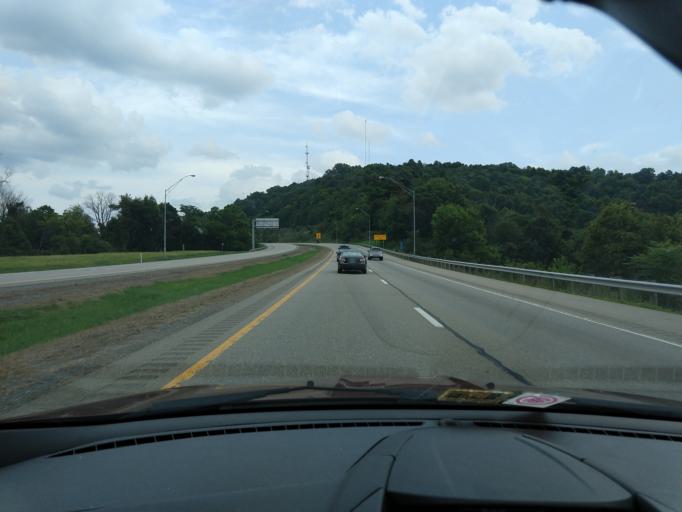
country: US
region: West Virginia
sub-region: Harrison County
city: Despard
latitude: 39.2764
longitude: -80.3022
